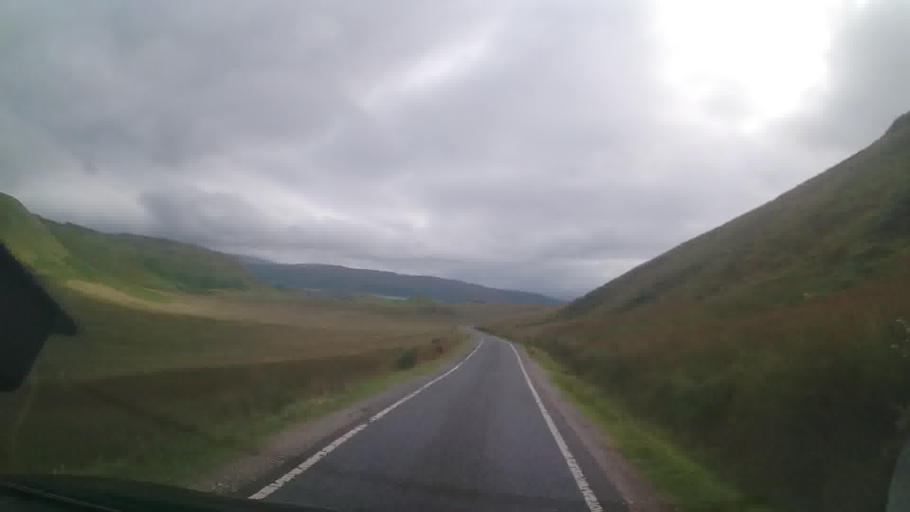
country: GB
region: Scotland
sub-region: Argyll and Bute
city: Isle Of Mull
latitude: 56.7018
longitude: -6.0015
